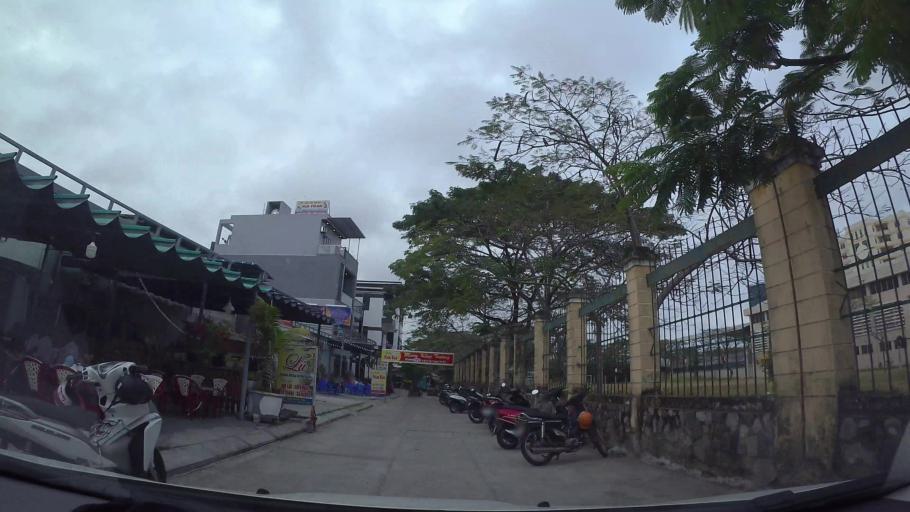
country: VN
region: Da Nang
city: Son Tra
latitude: 16.0578
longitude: 108.2324
